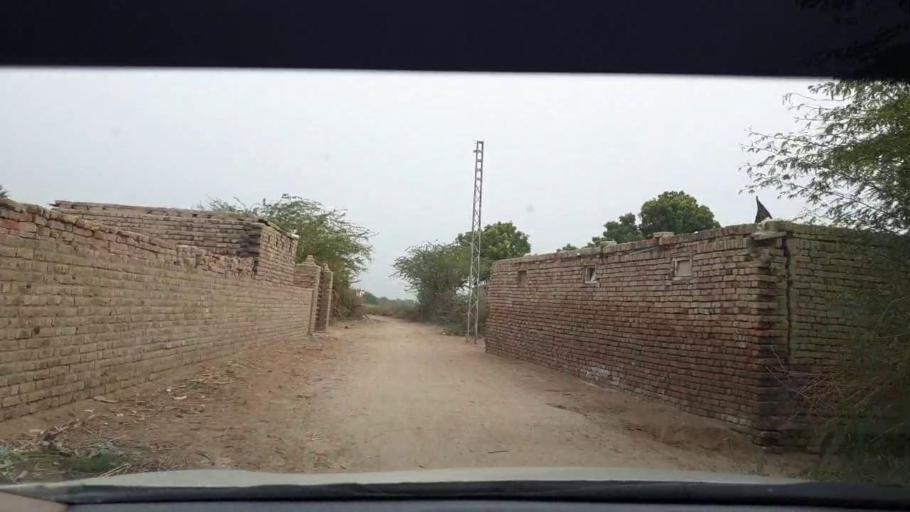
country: PK
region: Sindh
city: Berani
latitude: 25.8844
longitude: 68.8077
